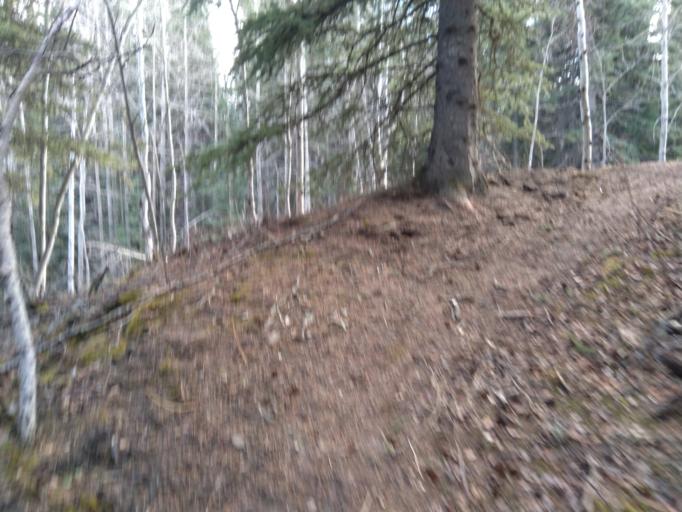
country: CA
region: Alberta
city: Cochrane
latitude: 51.1909
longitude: -114.5129
